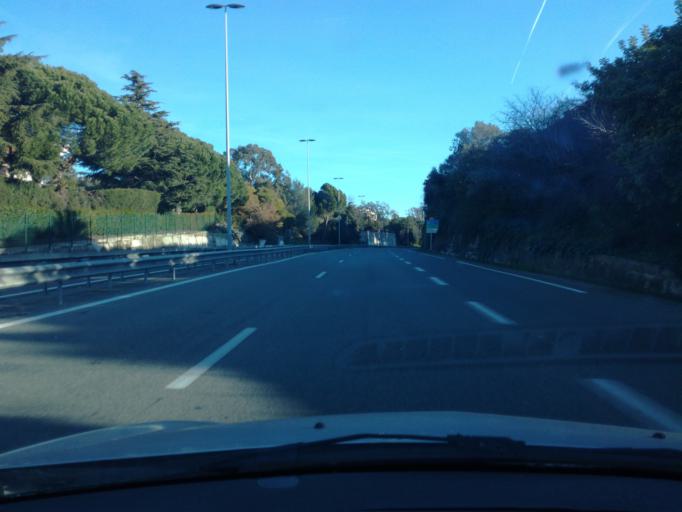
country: FR
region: Provence-Alpes-Cote d'Azur
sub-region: Departement des Alpes-Maritimes
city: Antibes
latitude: 43.5788
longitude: 7.1079
